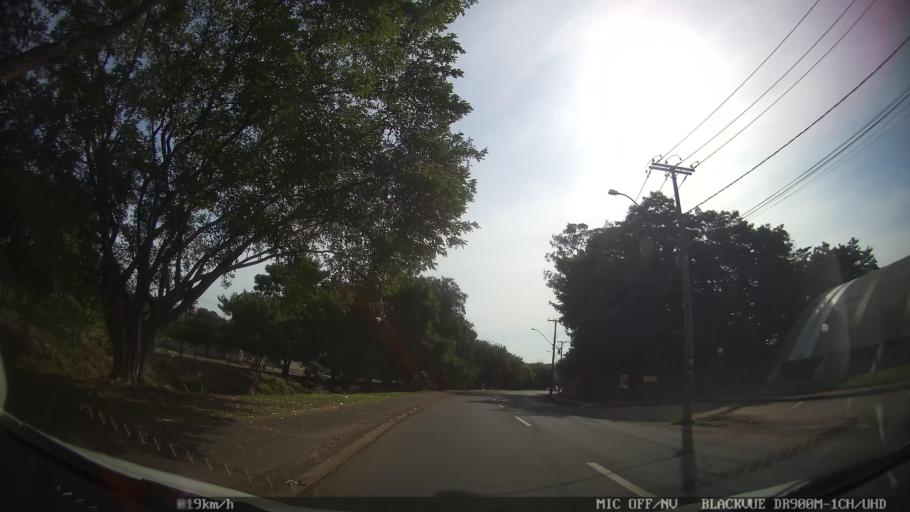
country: BR
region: Sao Paulo
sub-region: Piracicaba
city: Piracicaba
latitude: -22.7392
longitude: -47.6690
